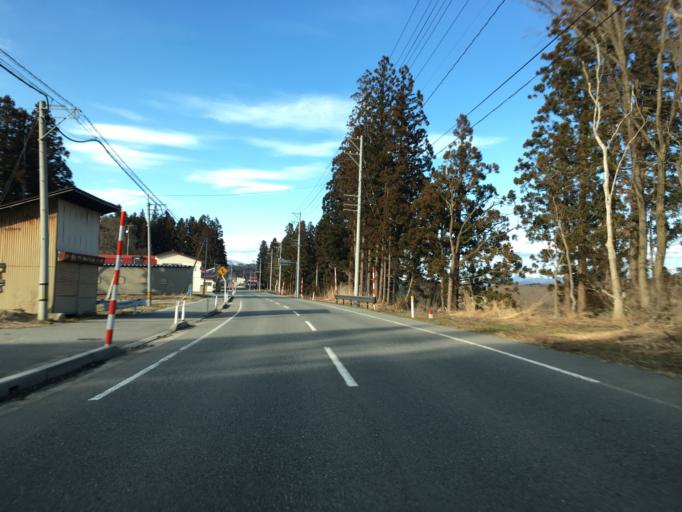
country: JP
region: Yamagata
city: Nagai
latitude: 38.0023
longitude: 139.9597
